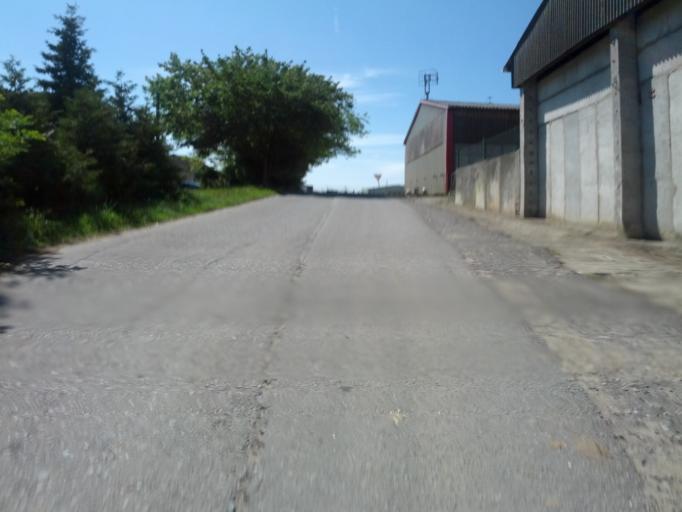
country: DE
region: Mecklenburg-Vorpommern
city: Bastorf
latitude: 54.1276
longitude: 11.6938
